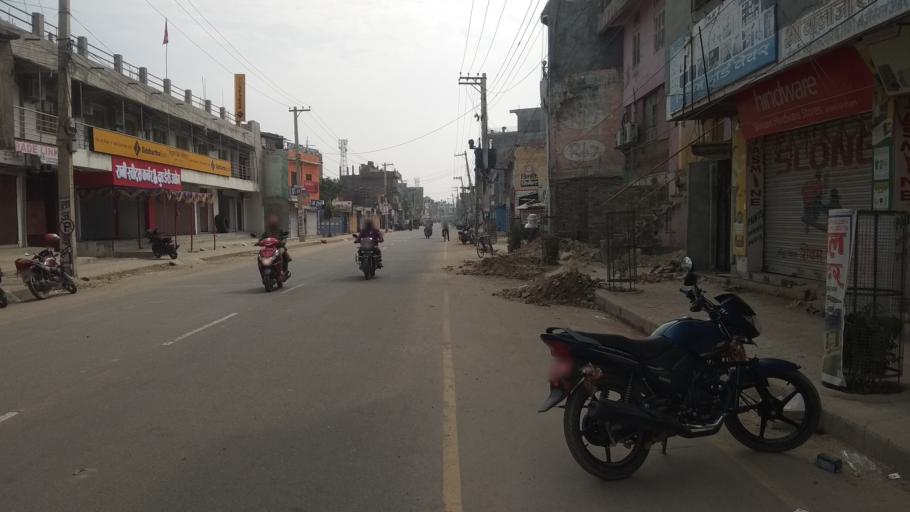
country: NP
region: Central Region
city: Janakpur
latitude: 26.7350
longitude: 85.9322
